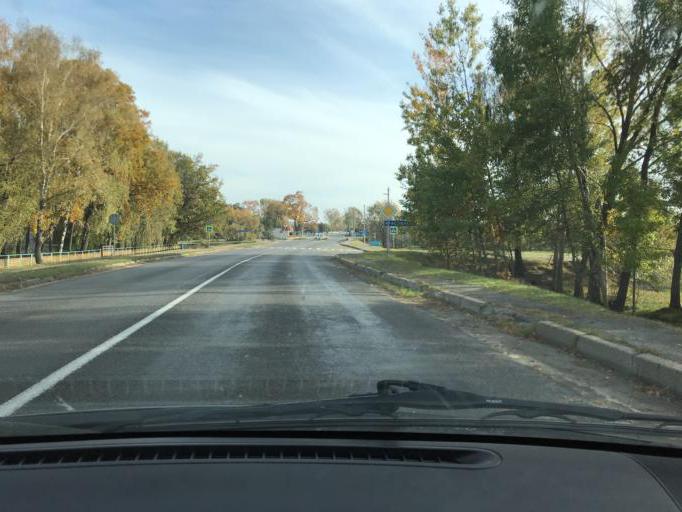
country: BY
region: Brest
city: Asnyezhytsy
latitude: 52.1984
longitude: 26.0663
